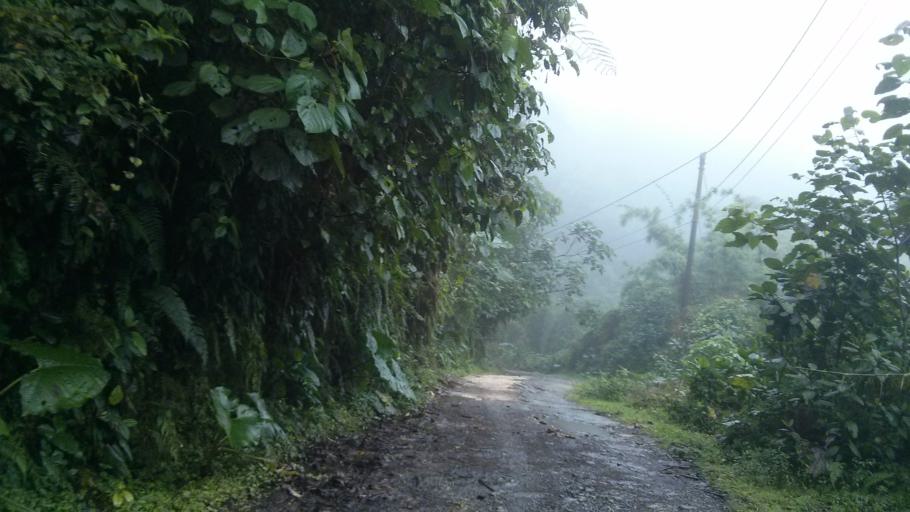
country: CR
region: San Jose
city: Ipis
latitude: 10.0312
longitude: -83.9379
